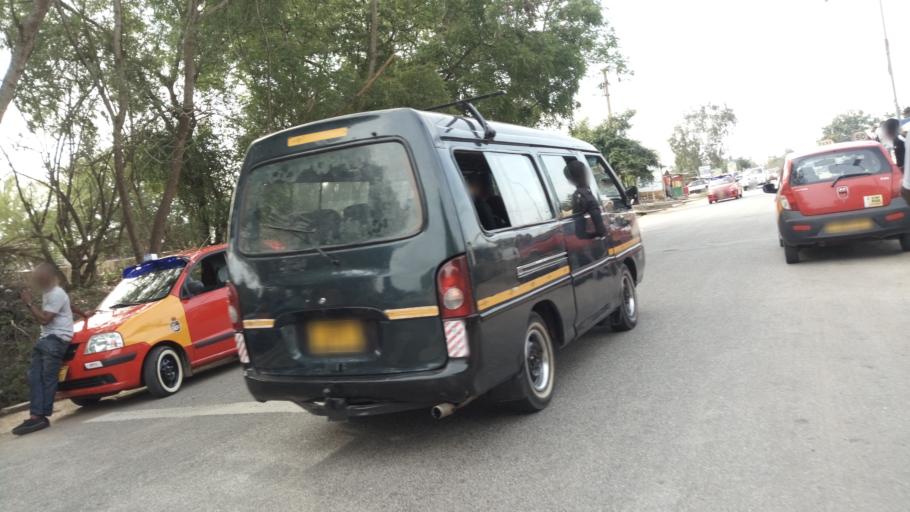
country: GH
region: Central
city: Winneba
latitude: 5.3840
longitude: -0.6429
